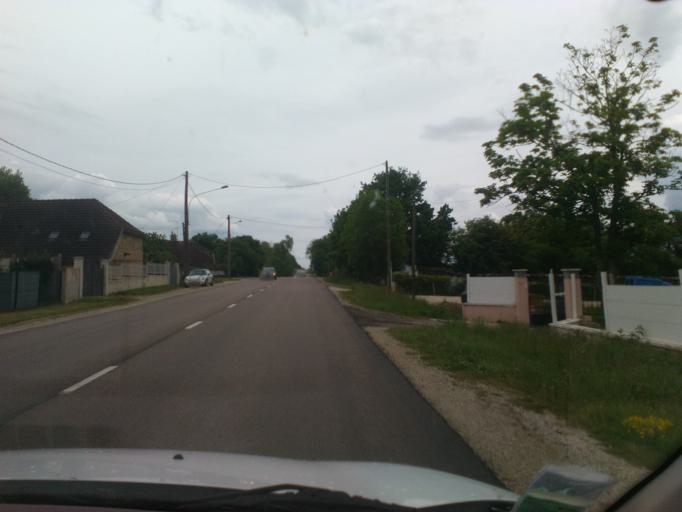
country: FR
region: Champagne-Ardenne
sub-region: Departement de l'Aube
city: Vendeuvre-sur-Barse
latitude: 48.2392
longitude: 4.3801
